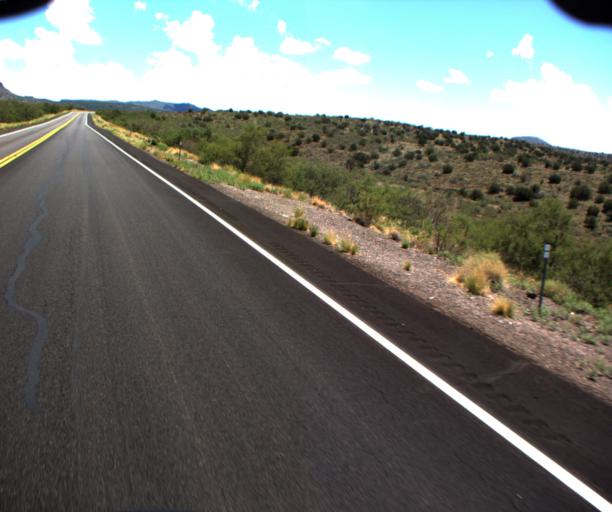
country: US
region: Arizona
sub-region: Yavapai County
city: Lake Montezuma
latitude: 34.5076
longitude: -111.7344
